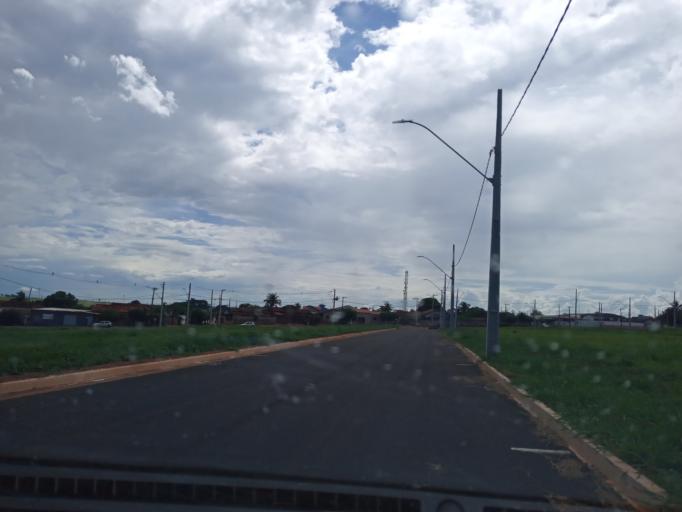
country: BR
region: Goias
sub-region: Itumbiara
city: Itumbiara
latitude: -18.4319
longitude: -49.1819
